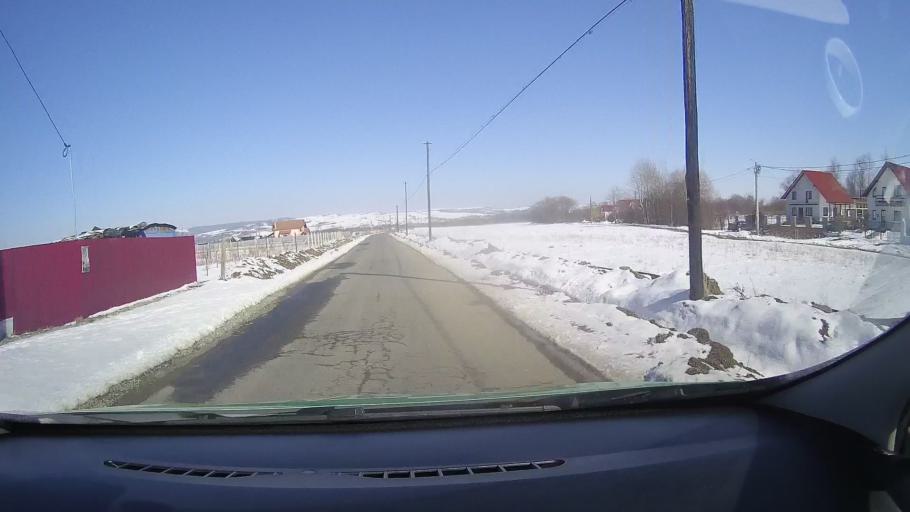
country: RO
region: Brasov
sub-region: Comuna Mandra
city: Mandra
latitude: 45.8262
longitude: 25.0099
